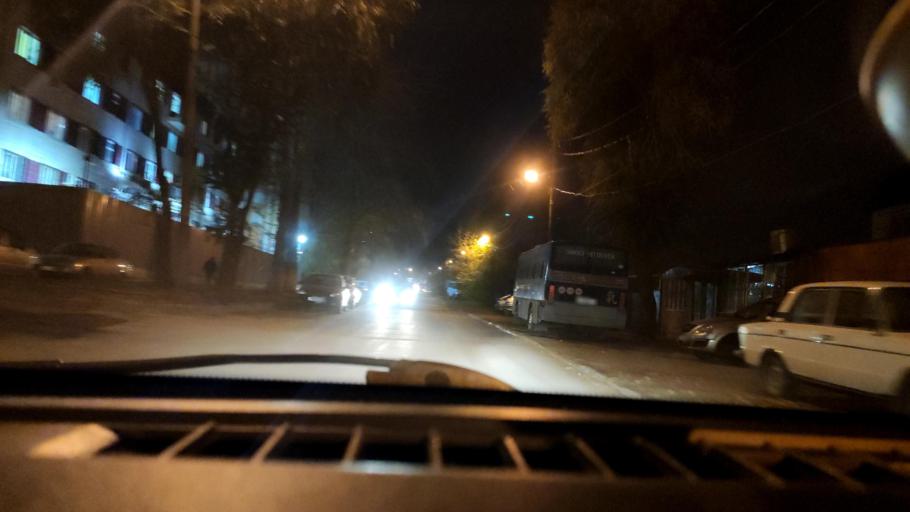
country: RU
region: Samara
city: Samara
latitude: 53.1892
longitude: 50.2184
